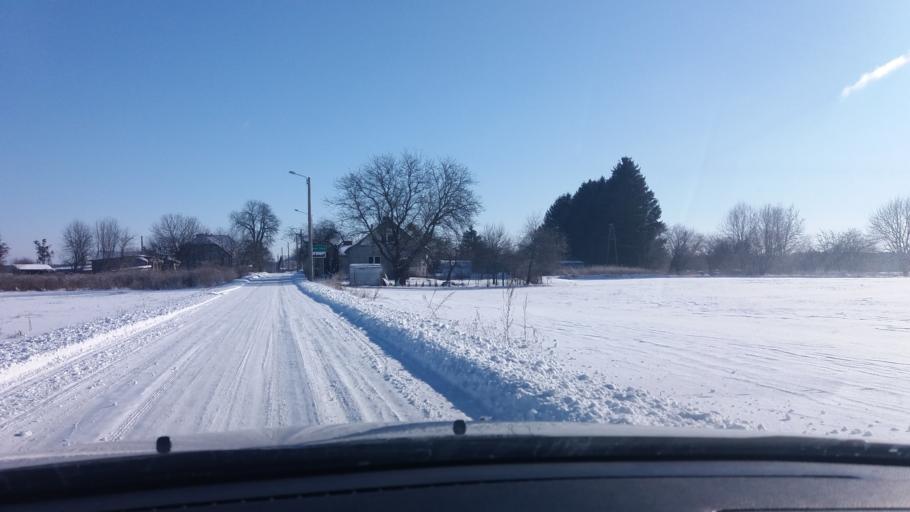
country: PL
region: Warmian-Masurian Voivodeship
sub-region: Powiat szczycienski
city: Szczytno
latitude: 53.5493
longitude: 20.9830
